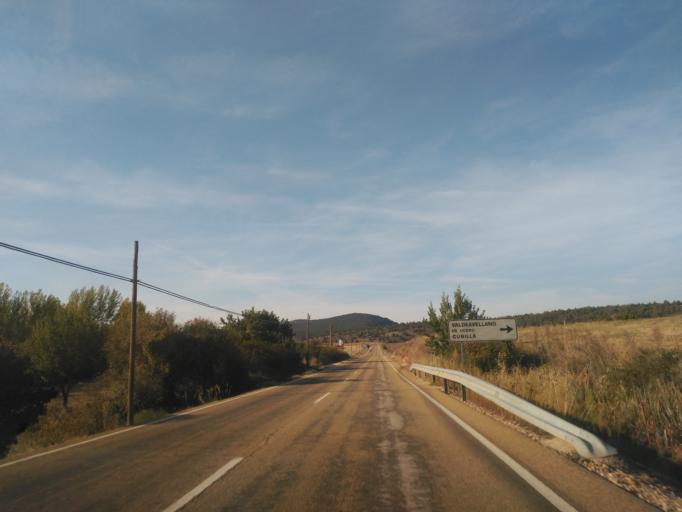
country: ES
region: Castille and Leon
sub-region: Provincia de Soria
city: Ucero
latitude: 41.7055
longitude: -3.0455
